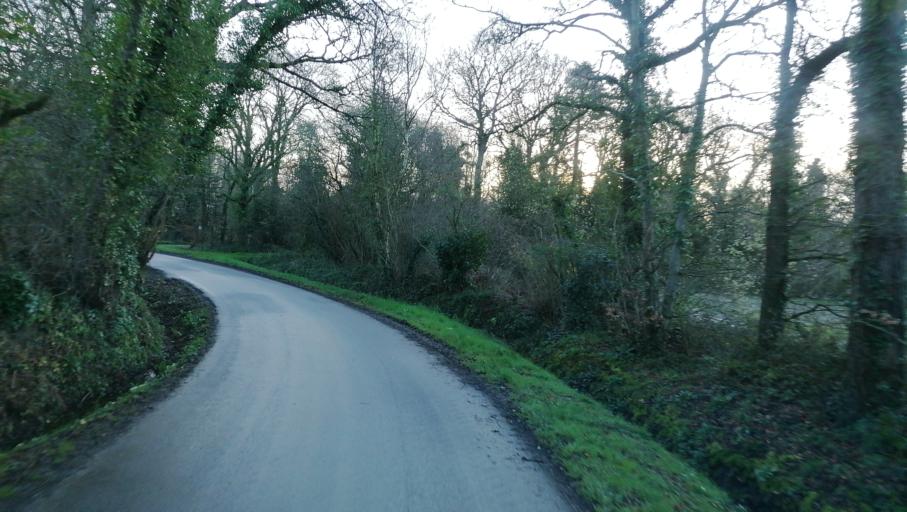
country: FR
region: Brittany
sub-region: Departement des Cotes-d'Armor
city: Pleguien
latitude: 48.6585
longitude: -2.9443
